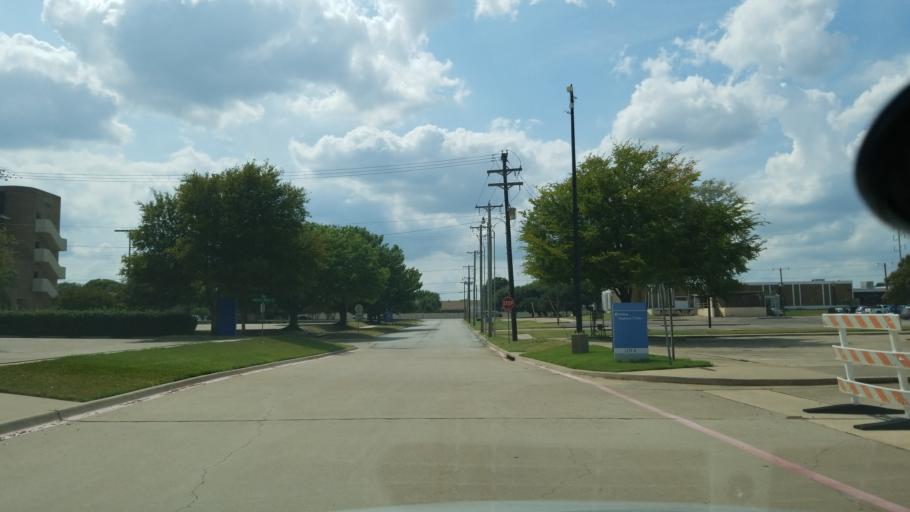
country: US
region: Texas
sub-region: Dallas County
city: Garland
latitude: 32.9205
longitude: -96.6630
